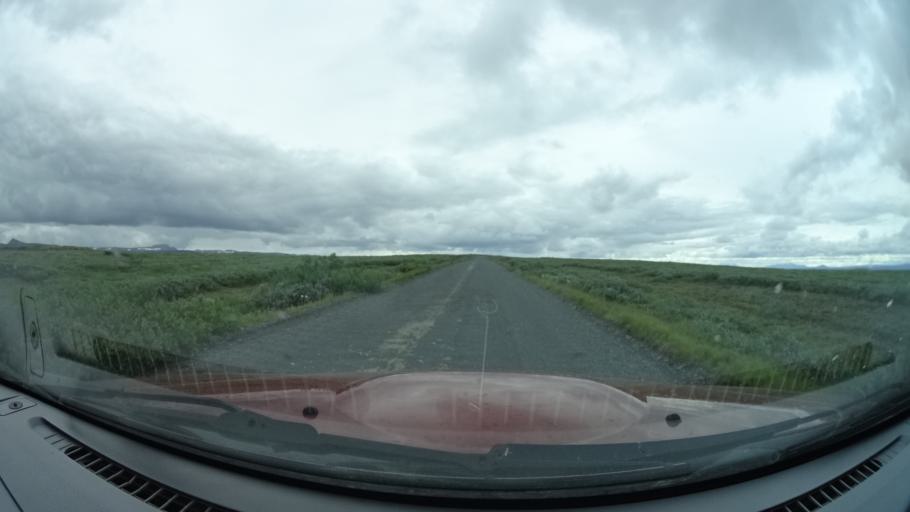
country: IS
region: Northeast
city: Laugar
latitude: 65.6798
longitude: -16.1725
